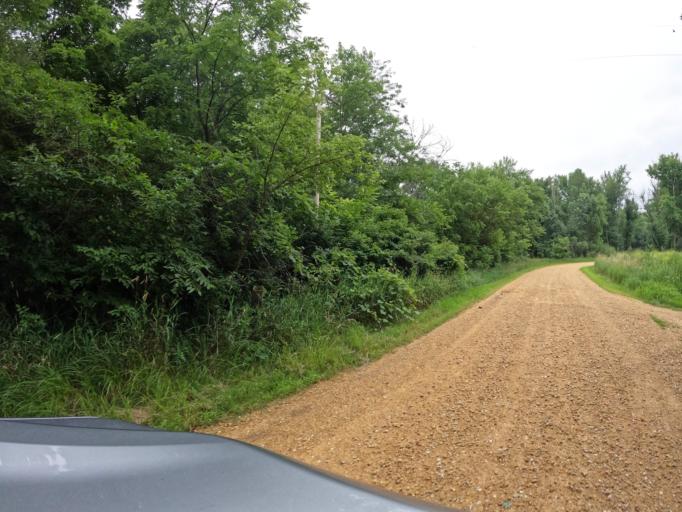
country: US
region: Illinois
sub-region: Carroll County
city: Savanna
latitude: 41.9834
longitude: -90.1714
